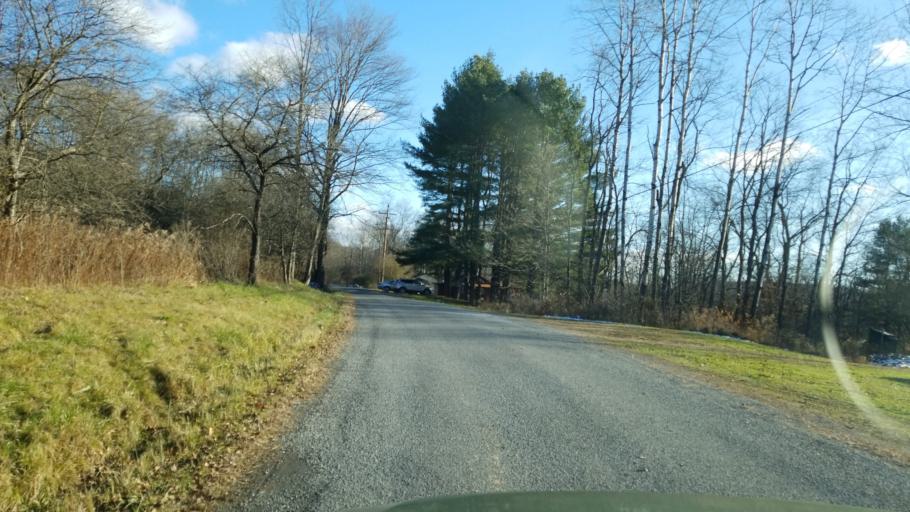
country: US
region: Pennsylvania
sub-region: Jefferson County
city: Brockway
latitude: 41.2618
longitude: -78.8033
